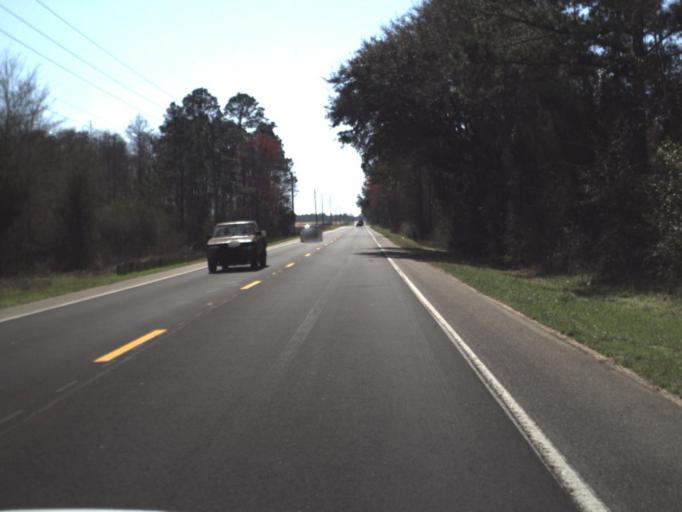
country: US
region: Florida
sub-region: Jackson County
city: Marianna
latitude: 30.6755
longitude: -85.1716
